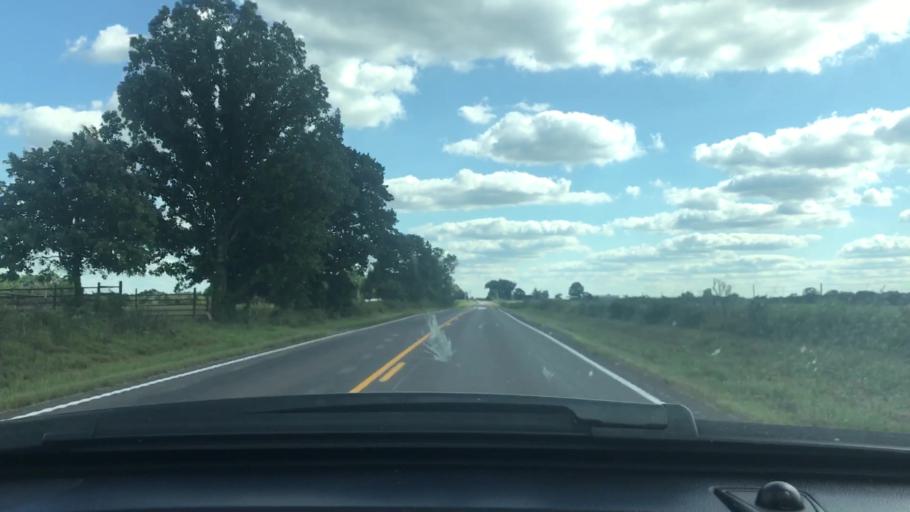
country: US
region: Missouri
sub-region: Wright County
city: Mountain Grove
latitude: 37.2690
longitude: -92.3081
